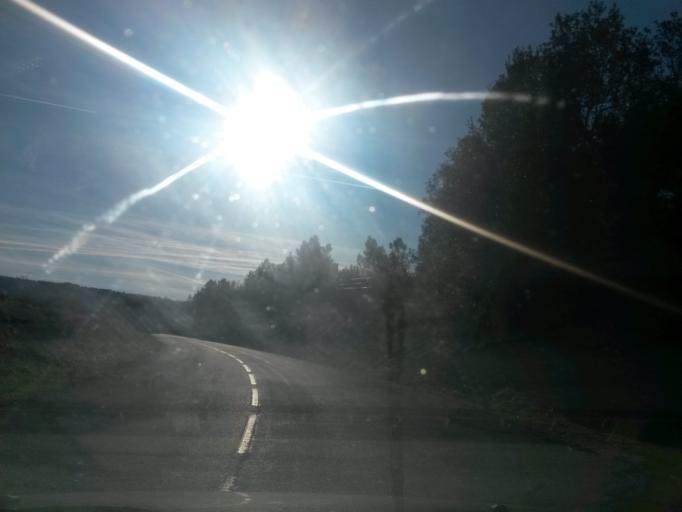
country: ES
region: Catalonia
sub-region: Provincia de Girona
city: Sant Gregori
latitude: 42.0250
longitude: 2.6760
